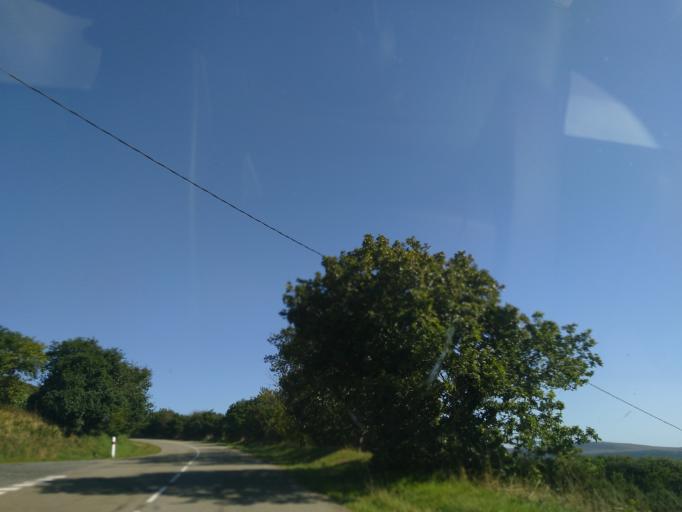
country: FR
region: Brittany
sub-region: Departement du Finistere
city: Hopital-Camfrout
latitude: 48.2719
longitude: -4.2605
